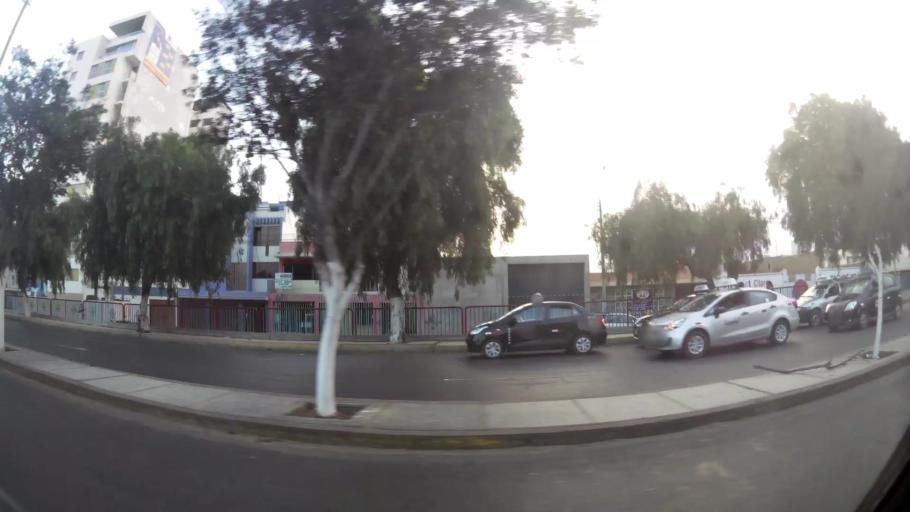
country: PE
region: La Libertad
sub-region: Provincia de Trujillo
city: Trujillo
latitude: -8.1004
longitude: -79.0366
